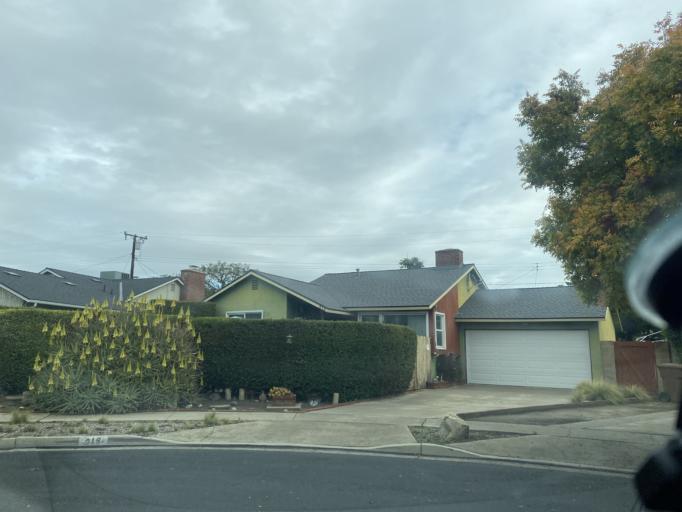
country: US
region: California
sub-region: Orange County
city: Fullerton
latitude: 33.8688
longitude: -117.9025
